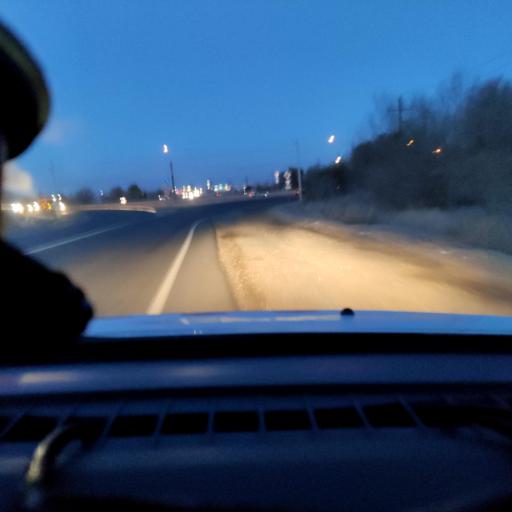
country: RU
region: Samara
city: Samara
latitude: 53.1262
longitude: 50.1732
